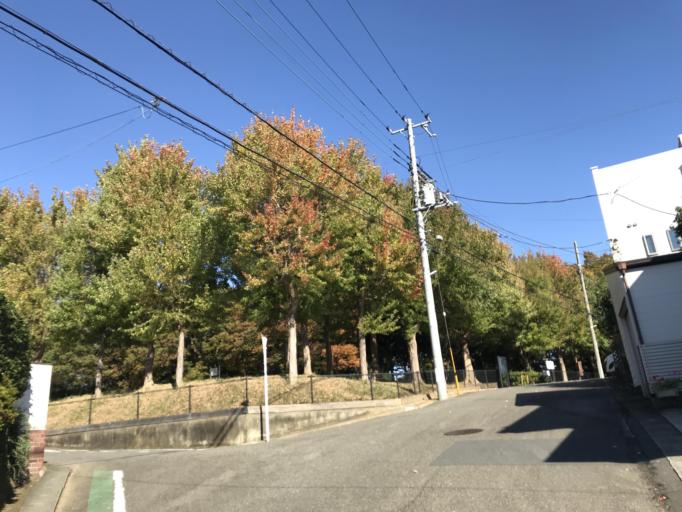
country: JP
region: Tokyo
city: Chofugaoka
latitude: 35.5745
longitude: 139.5790
